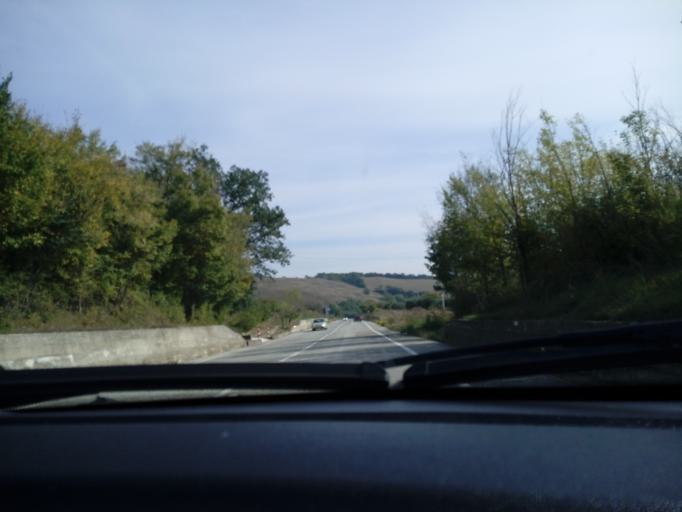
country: IT
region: Molise
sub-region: Provincia di Campobasso
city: Riccia
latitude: 41.5234
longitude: 14.8539
